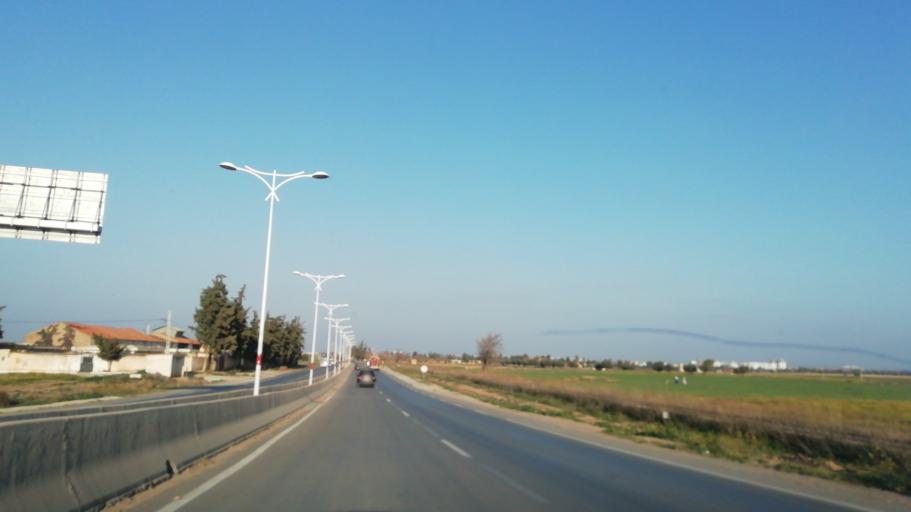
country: DZ
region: Sidi Bel Abbes
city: Sidi Bel Abbes
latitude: 35.1702
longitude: -0.6810
